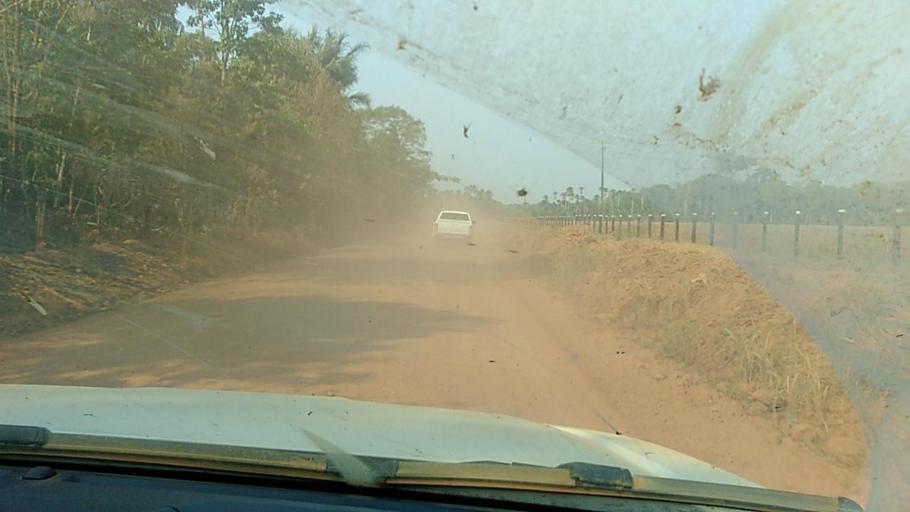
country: BR
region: Rondonia
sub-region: Porto Velho
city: Porto Velho
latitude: -8.7848
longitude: -64.0907
